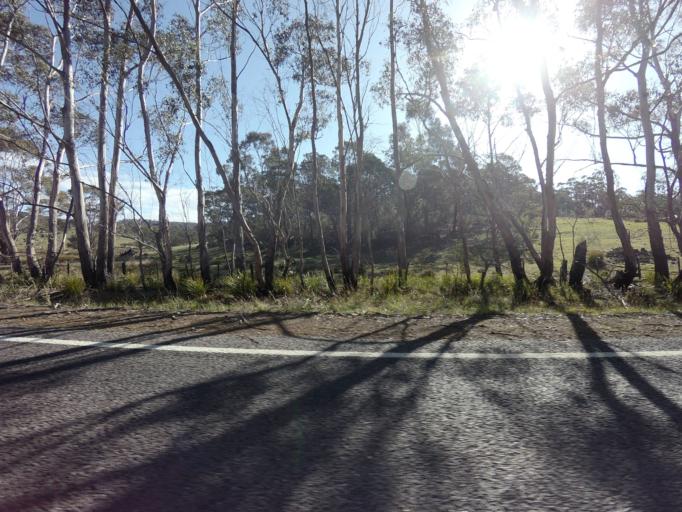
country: AU
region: Tasmania
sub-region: Sorell
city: Sorell
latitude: -42.4129
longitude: 147.9341
